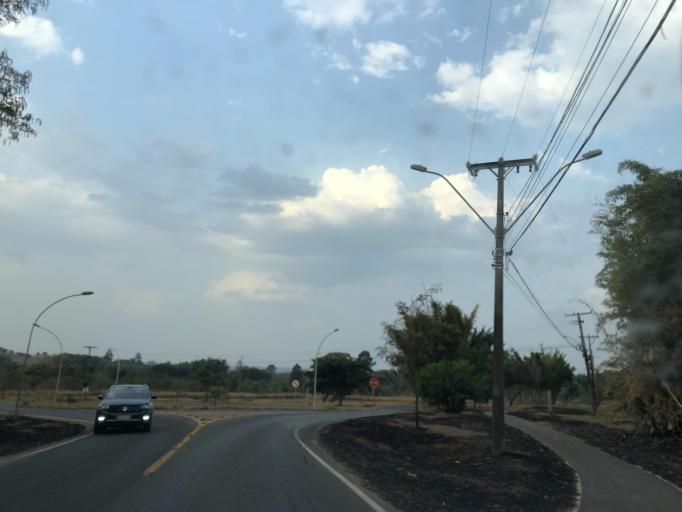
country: BR
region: Federal District
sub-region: Brasilia
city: Brasilia
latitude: -15.9391
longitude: -47.9756
